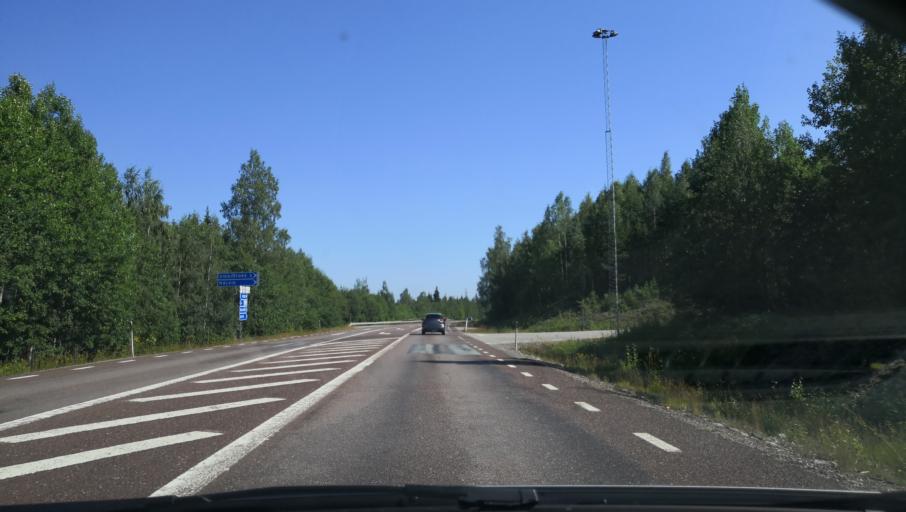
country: SE
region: Gaevleborg
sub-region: Ovanakers Kommun
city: Alfta
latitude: 61.3442
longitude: 16.0126
